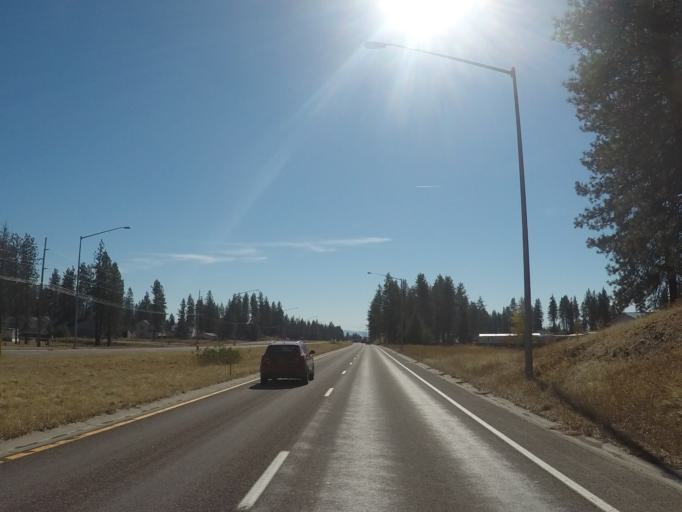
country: US
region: Montana
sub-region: Lake County
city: Pablo
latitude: 47.6088
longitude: -114.1132
